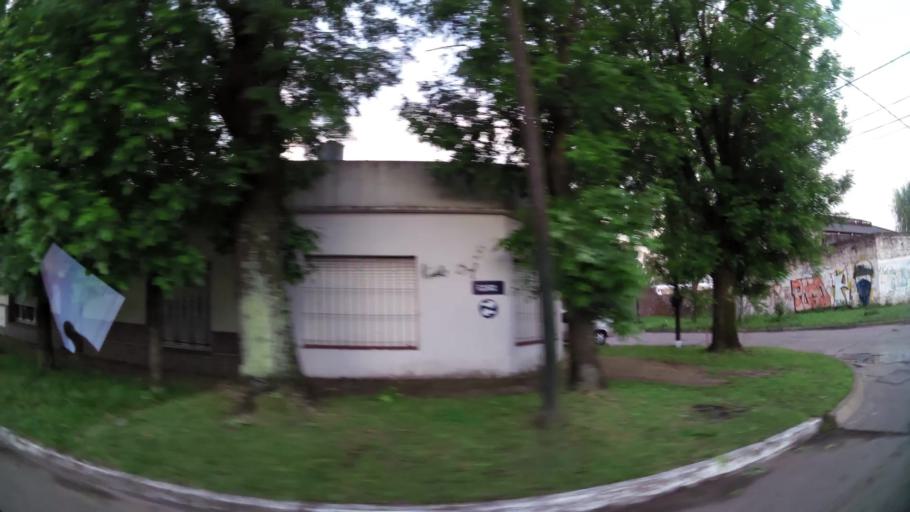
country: AR
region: Buenos Aires
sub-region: Partido de Lomas de Zamora
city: Lomas de Zamora
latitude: -34.7599
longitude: -58.3770
